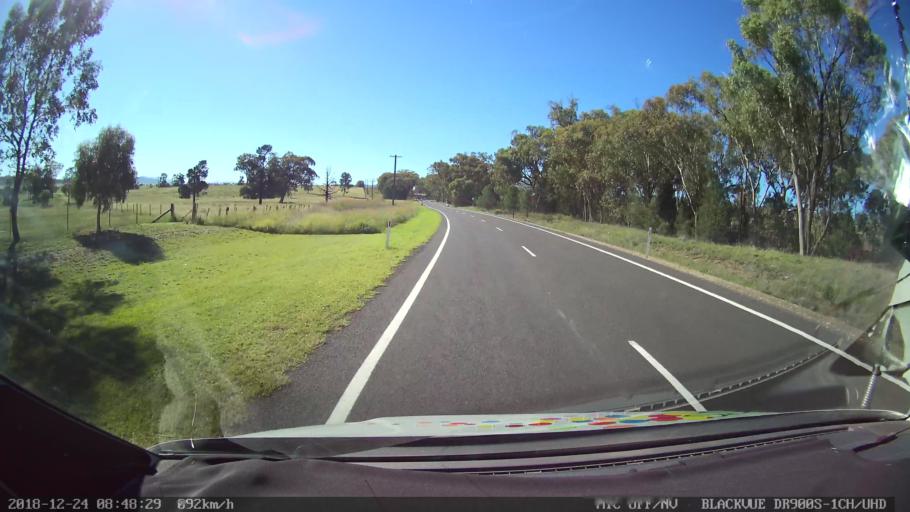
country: AU
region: New South Wales
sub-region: Liverpool Plains
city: Quirindi
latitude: -31.4563
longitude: 150.6463
